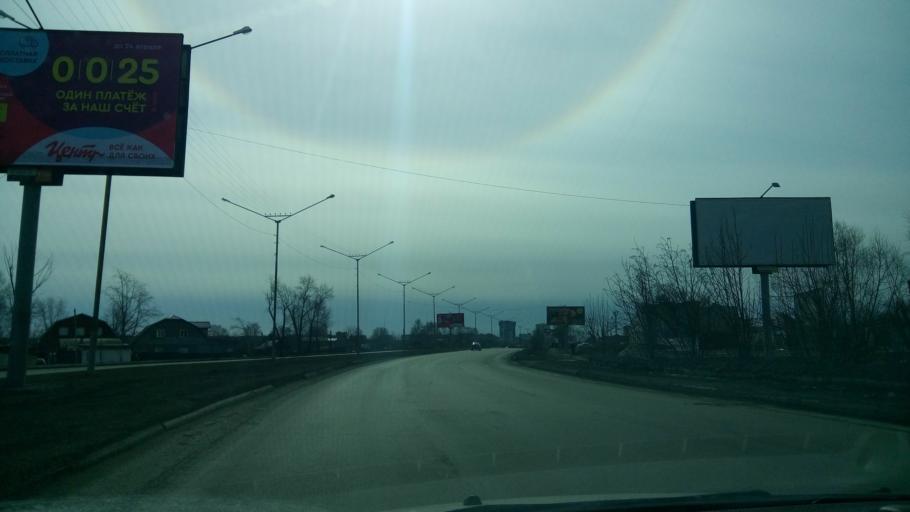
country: RU
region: Sverdlovsk
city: Nizhniy Tagil
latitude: 57.8962
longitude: 59.9405
